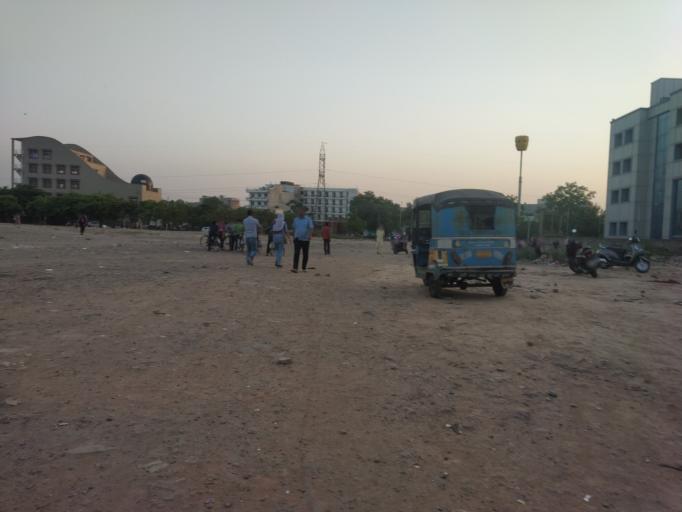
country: IN
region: Punjab
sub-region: Ajitgarh
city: Mohali
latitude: 30.6904
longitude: 76.7294
